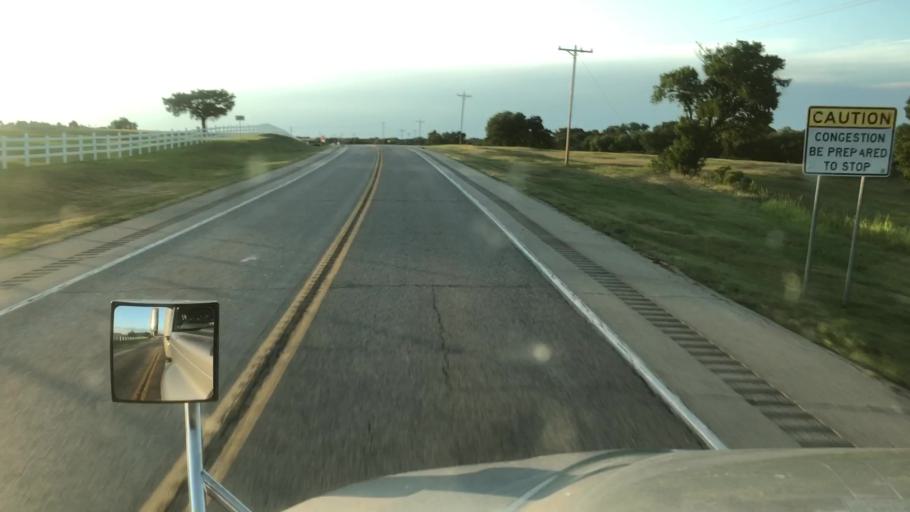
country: US
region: Oklahoma
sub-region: Osage County
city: McCord
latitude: 36.4843
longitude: -97.0698
